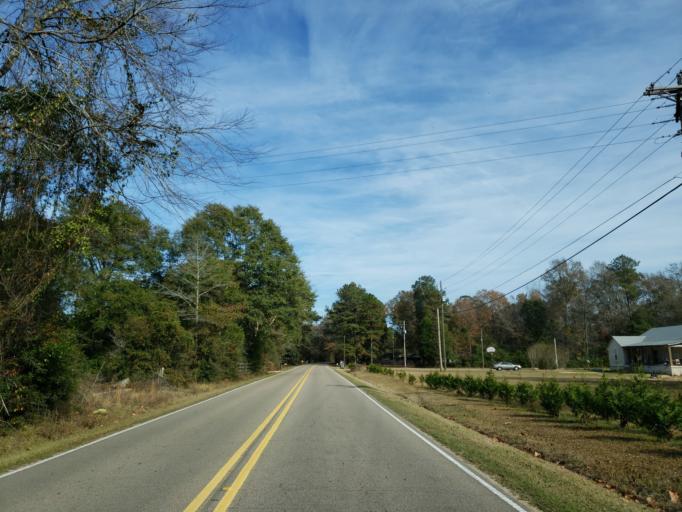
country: US
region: Mississippi
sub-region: Forrest County
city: Rawls Springs
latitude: 31.3917
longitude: -89.3753
